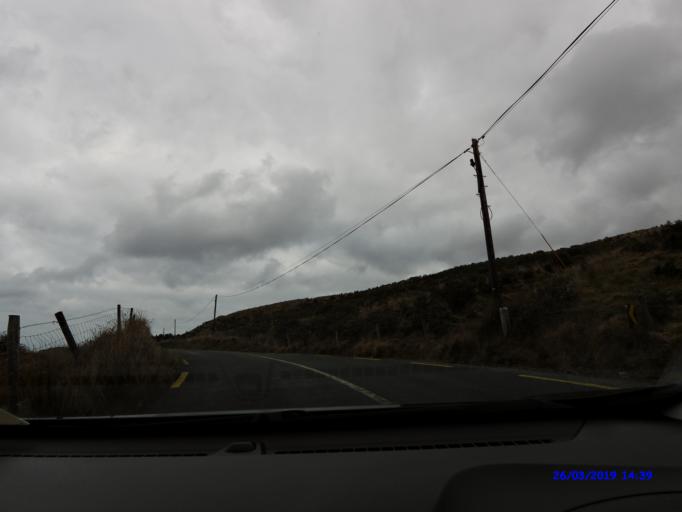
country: IE
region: Connaught
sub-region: Maigh Eo
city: Crossmolina
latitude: 54.3064
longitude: -9.5016
